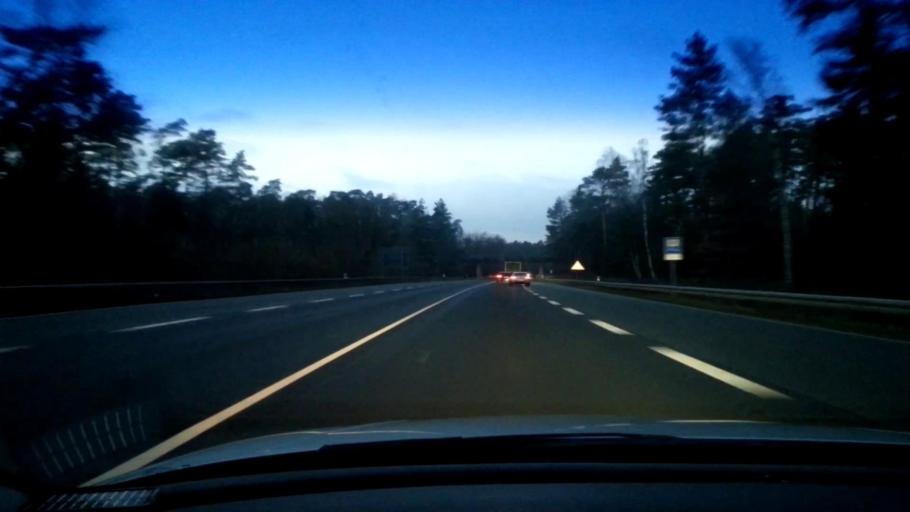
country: DE
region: Bavaria
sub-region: Upper Franconia
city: Strullendorf
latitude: 49.8672
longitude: 10.9467
